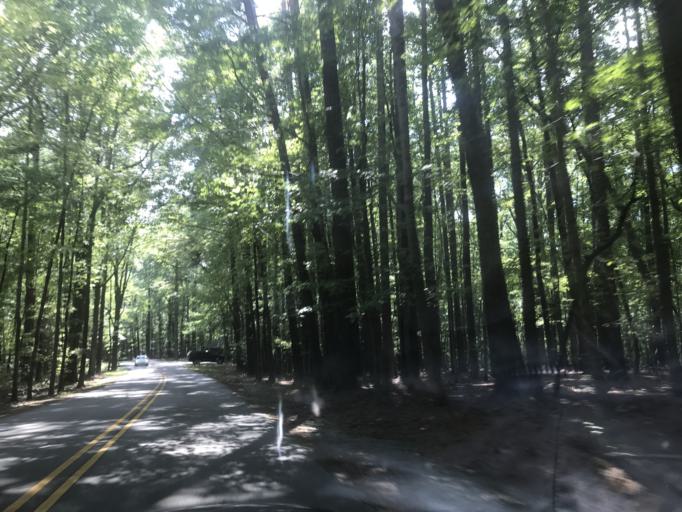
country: US
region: North Carolina
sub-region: Wake County
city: Morrisville
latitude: 35.8894
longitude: -78.7525
